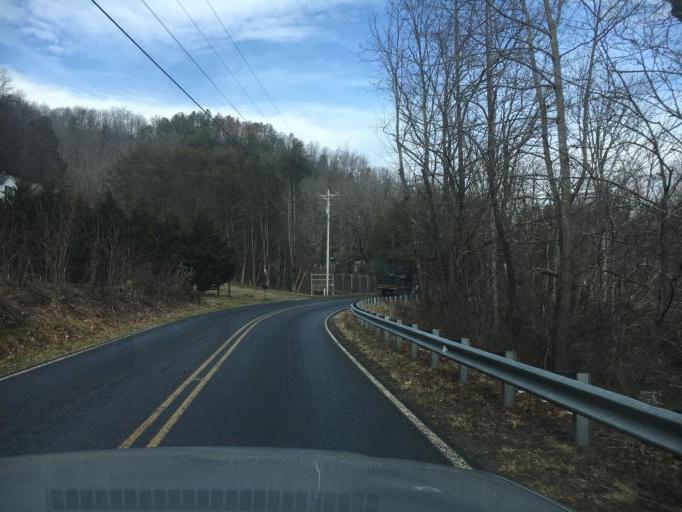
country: US
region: North Carolina
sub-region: Haywood County
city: Canton
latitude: 35.4075
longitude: -82.8134
